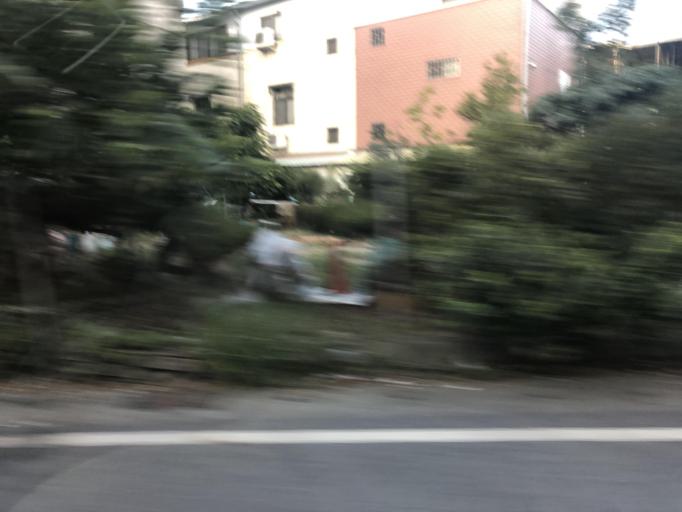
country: TW
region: Taiwan
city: Xinying
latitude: 23.1778
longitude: 120.2531
